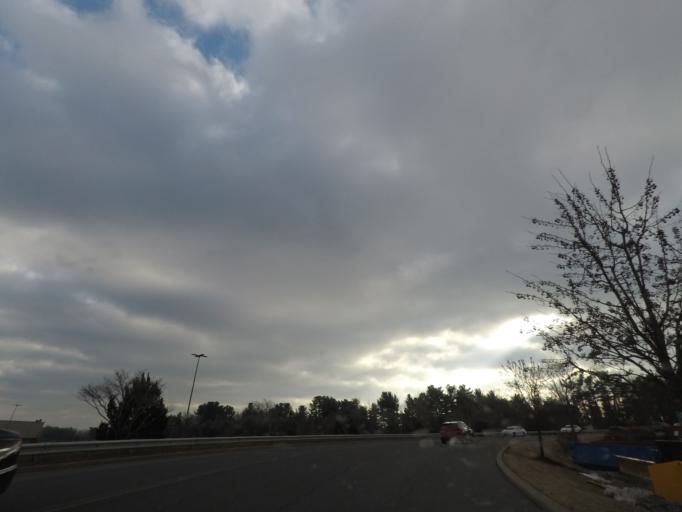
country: US
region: New York
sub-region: Albany County
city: McKownville
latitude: 42.6915
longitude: -73.8560
